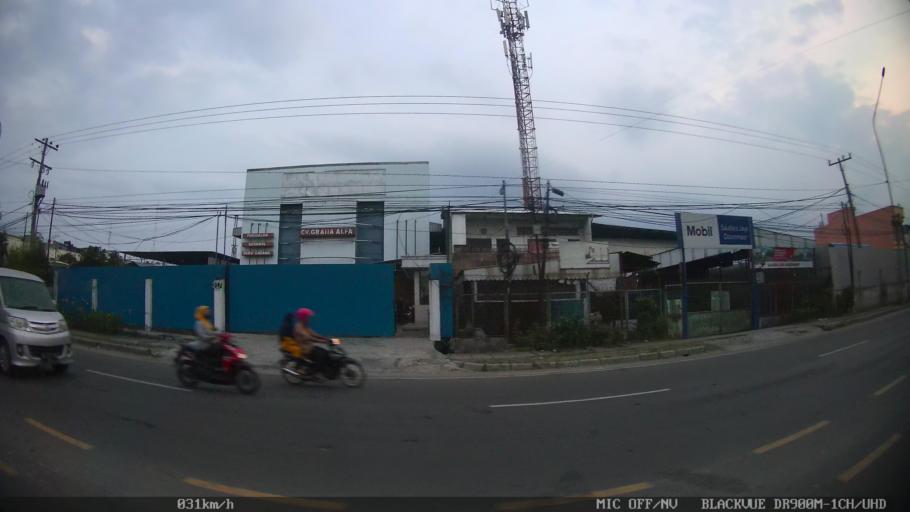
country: ID
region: North Sumatra
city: Sunggal
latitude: 3.5964
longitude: 98.6129
